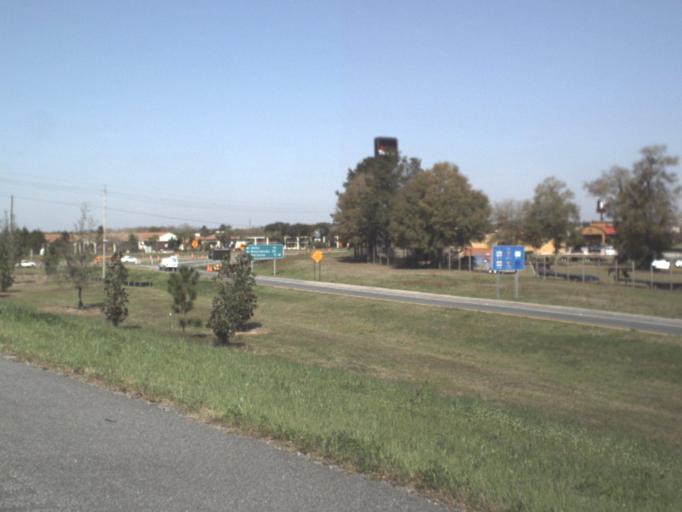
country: US
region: Florida
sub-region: Jackson County
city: Marianna
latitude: 30.7211
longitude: -85.1835
